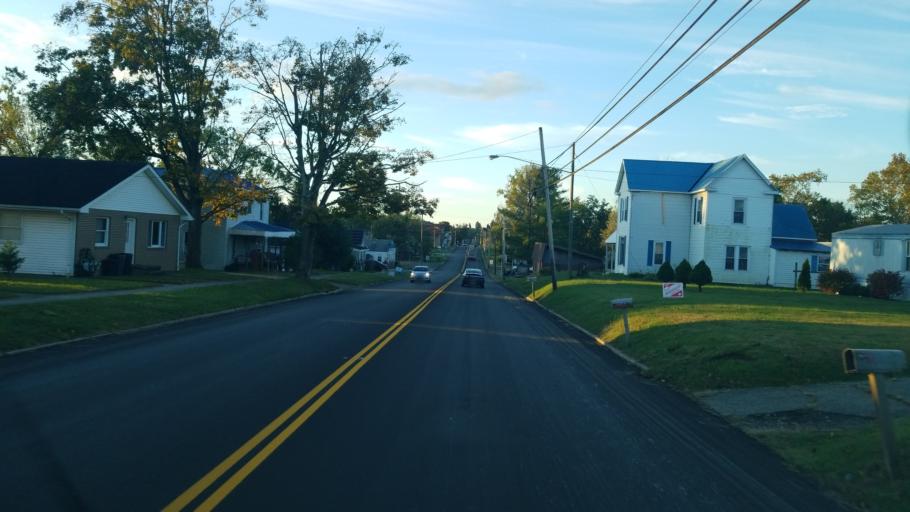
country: US
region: Ohio
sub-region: Jackson County
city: Wellston
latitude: 39.1628
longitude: -82.5268
